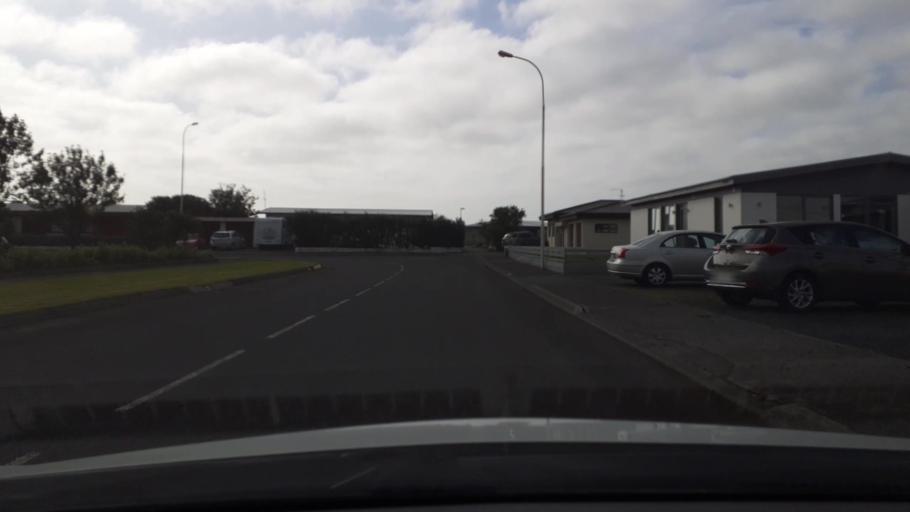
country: IS
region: South
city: THorlakshoefn
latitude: 63.8528
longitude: -21.3915
